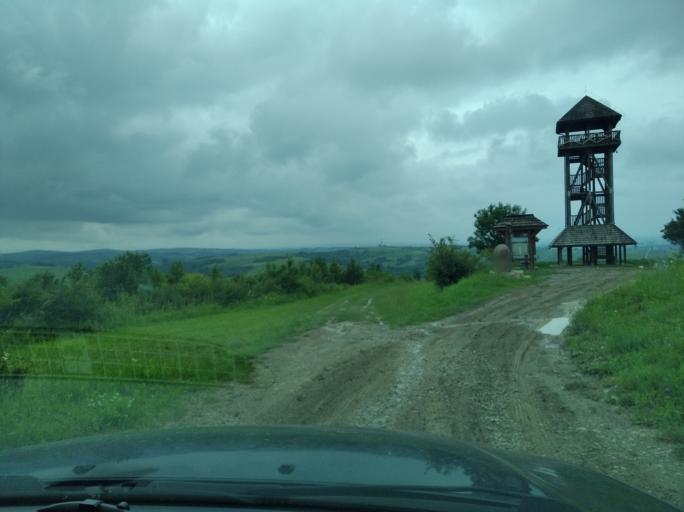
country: PL
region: Subcarpathian Voivodeship
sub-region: Powiat jaroslawski
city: Pruchnik
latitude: 49.8884
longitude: 22.5125
